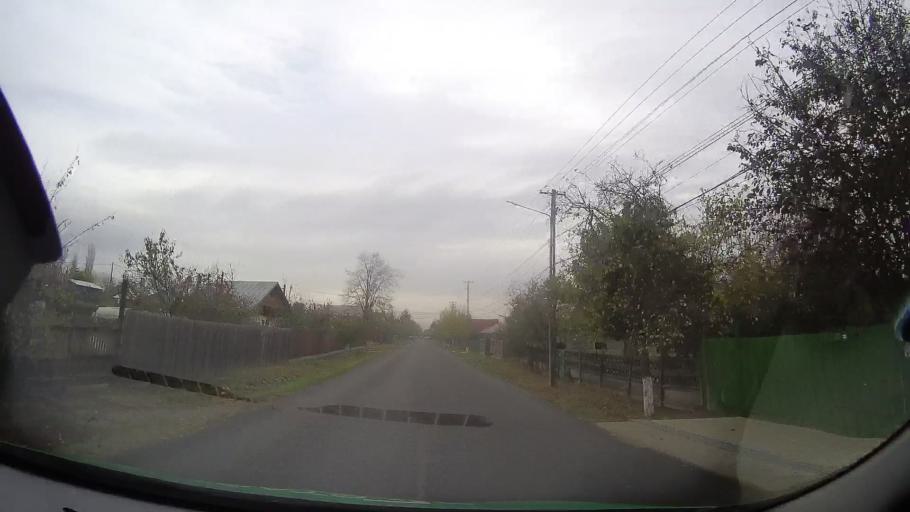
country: RO
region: Prahova
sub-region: Comuna Valea Calugareasca
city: Pantazi
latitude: 44.9382
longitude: 26.1365
